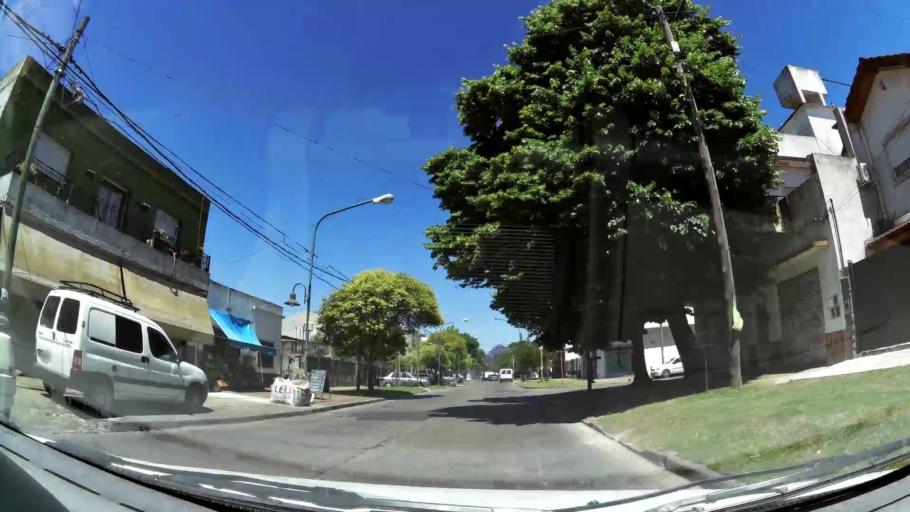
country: AR
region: Buenos Aires
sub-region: Partido de Vicente Lopez
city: Olivos
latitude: -34.5169
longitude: -58.5349
